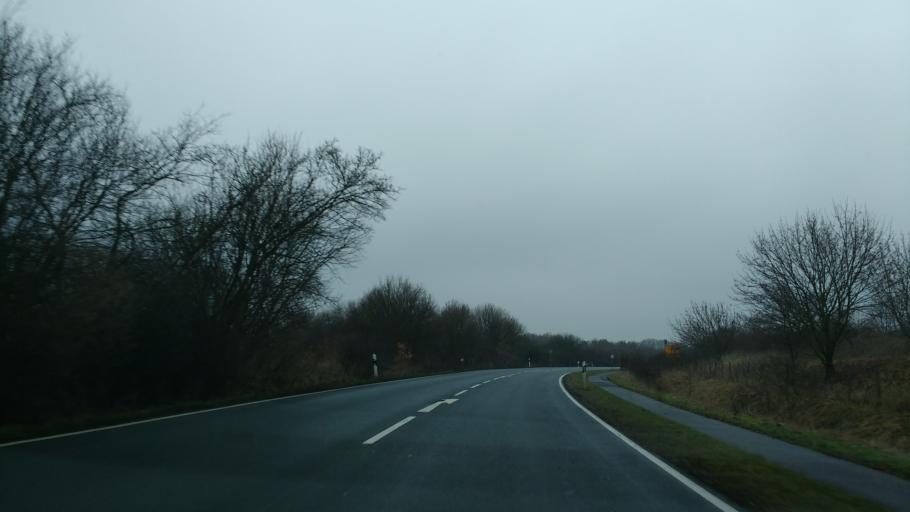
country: DE
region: Lower Saxony
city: Garbsen
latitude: 52.4297
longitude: 9.5724
